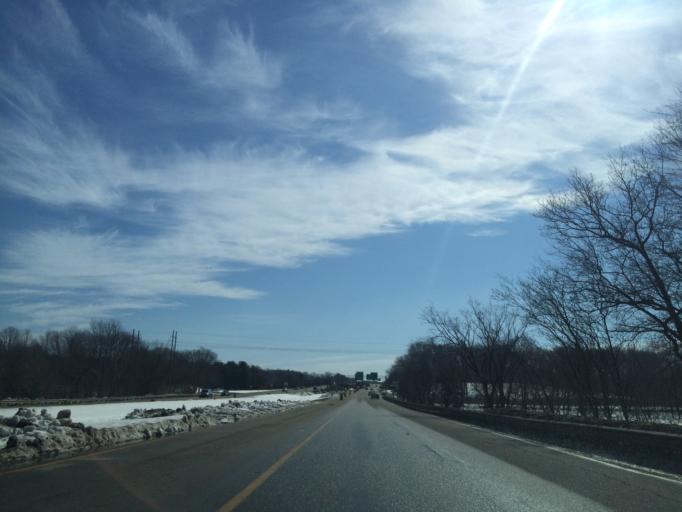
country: US
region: Massachusetts
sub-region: Middlesex County
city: Lincoln
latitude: 42.4311
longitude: -71.2647
